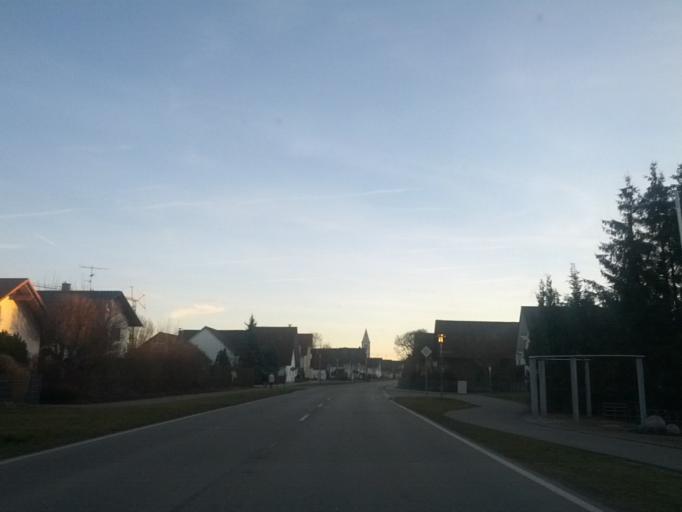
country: DE
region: Baden-Wuerttemberg
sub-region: Tuebingen Region
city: Berkheim
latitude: 48.0456
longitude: 10.0811
